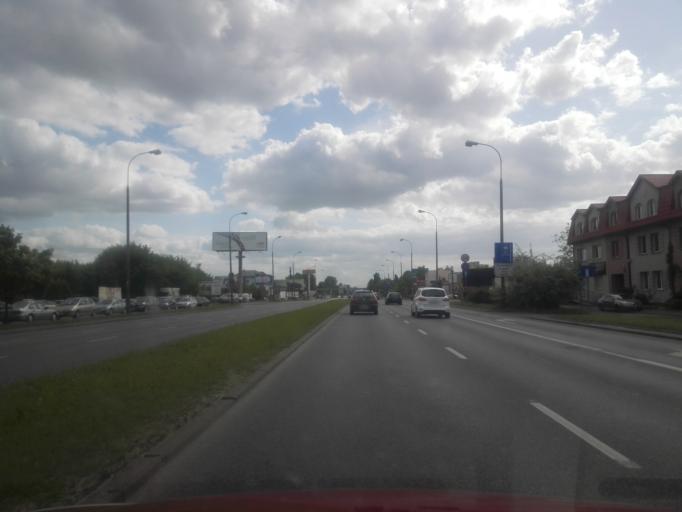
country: PL
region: Masovian Voivodeship
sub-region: Warszawa
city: Targowek
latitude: 52.2792
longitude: 21.0689
